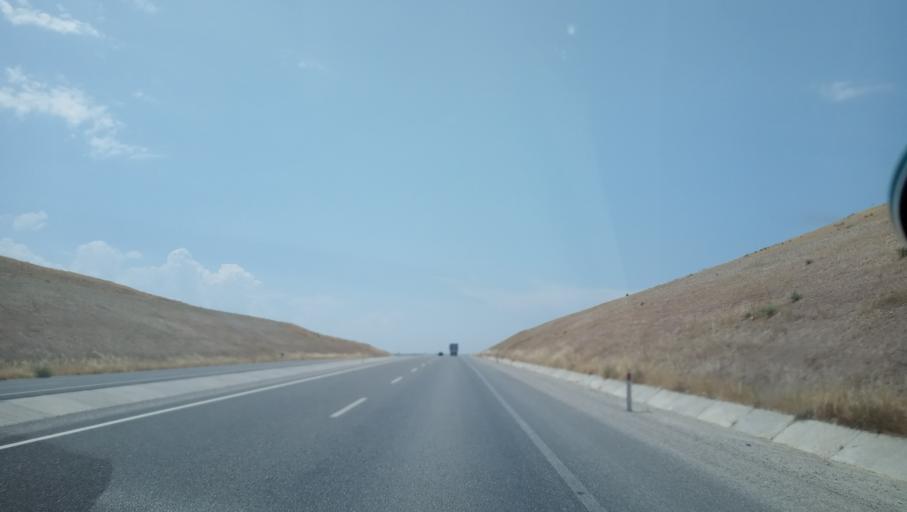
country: TR
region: Diyarbakir
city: Salat
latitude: 37.8609
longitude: 40.8700
